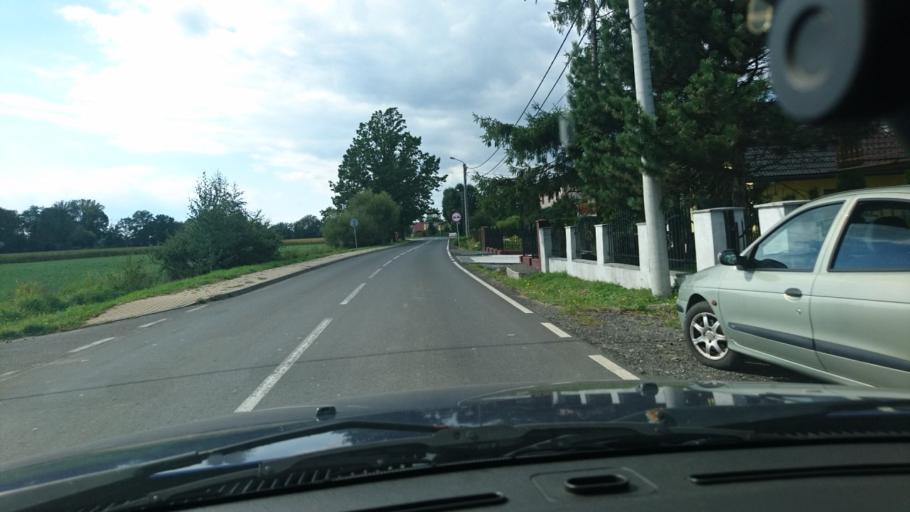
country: PL
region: Silesian Voivodeship
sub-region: Powiat bielski
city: Ligota
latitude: 49.8989
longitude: 18.9592
